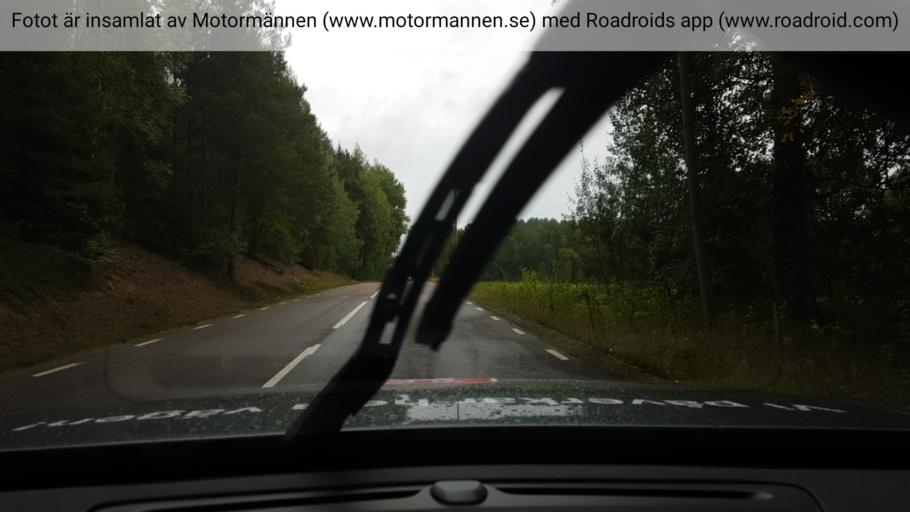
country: SE
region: Stockholm
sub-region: Botkyrka Kommun
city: Varsta
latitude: 59.1153
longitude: 17.8594
